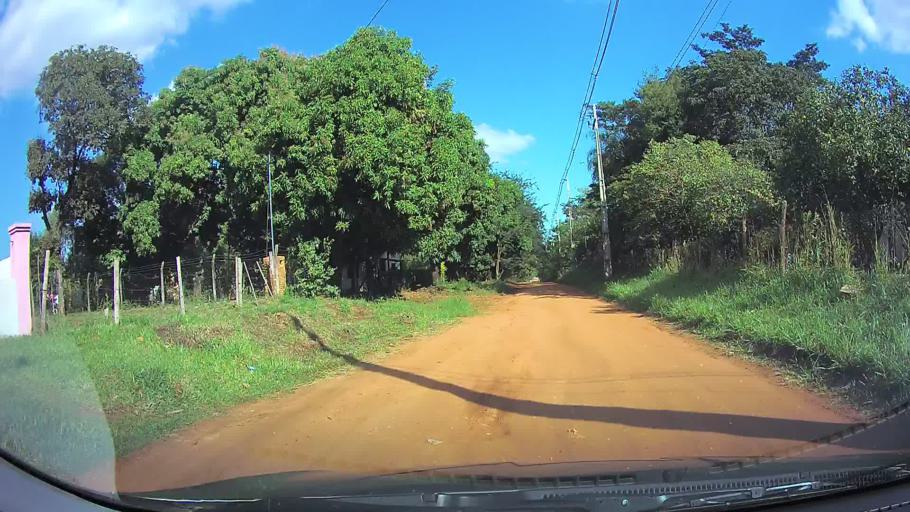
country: PY
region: Central
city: Limpio
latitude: -25.2493
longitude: -57.4748
